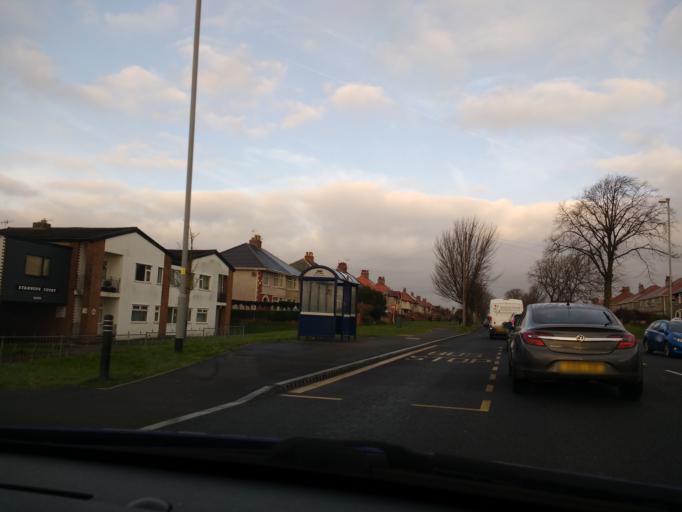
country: GB
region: England
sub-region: Lancashire
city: Morecambe
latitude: 54.0635
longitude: -2.8325
